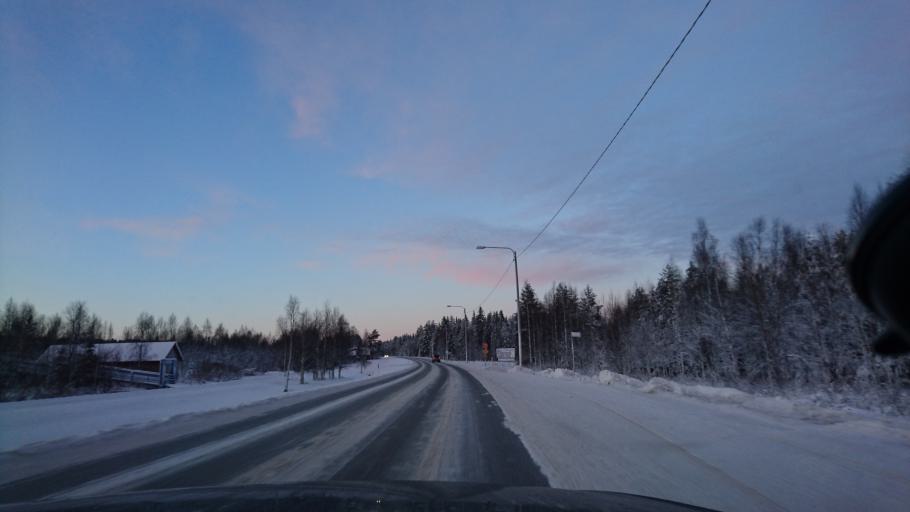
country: FI
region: Lapland
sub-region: Rovaniemi
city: Ranua
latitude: 65.9374
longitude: 26.4890
